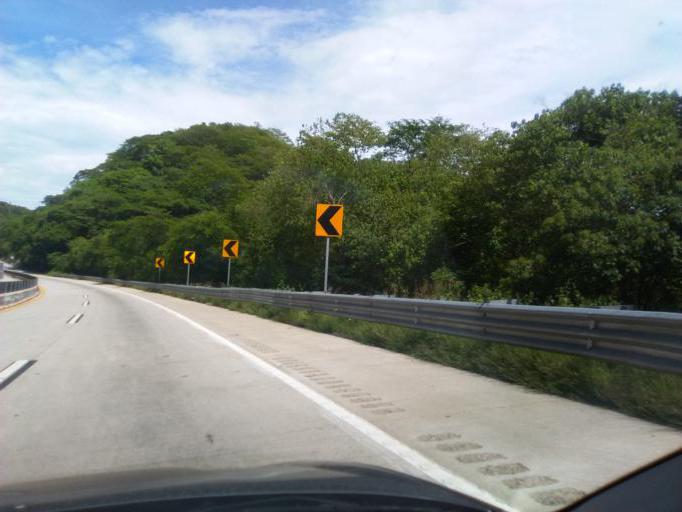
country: MX
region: Guerrero
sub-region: Acapulco de Juarez
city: Pueblo Madero (El Playon)
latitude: 17.0750
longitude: -99.6068
